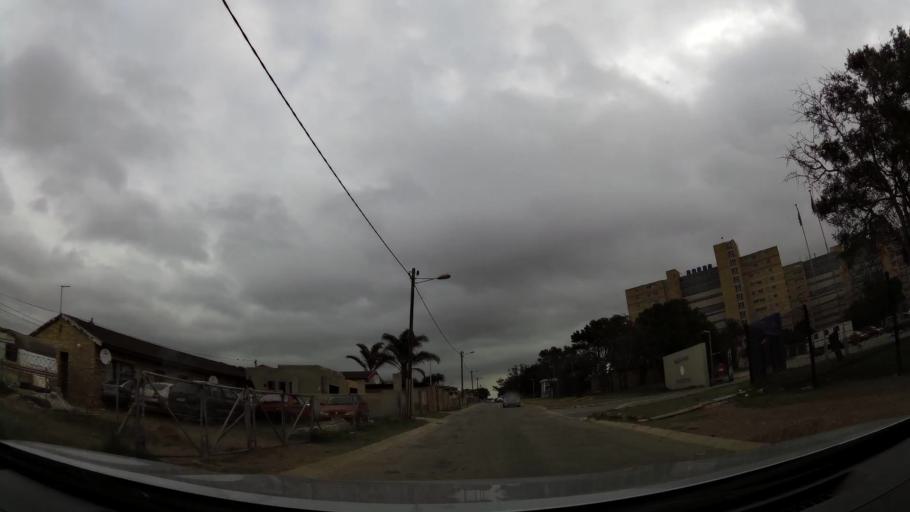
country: ZA
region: Eastern Cape
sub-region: Nelson Mandela Bay Metropolitan Municipality
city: Port Elizabeth
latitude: -33.9034
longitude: 25.5704
